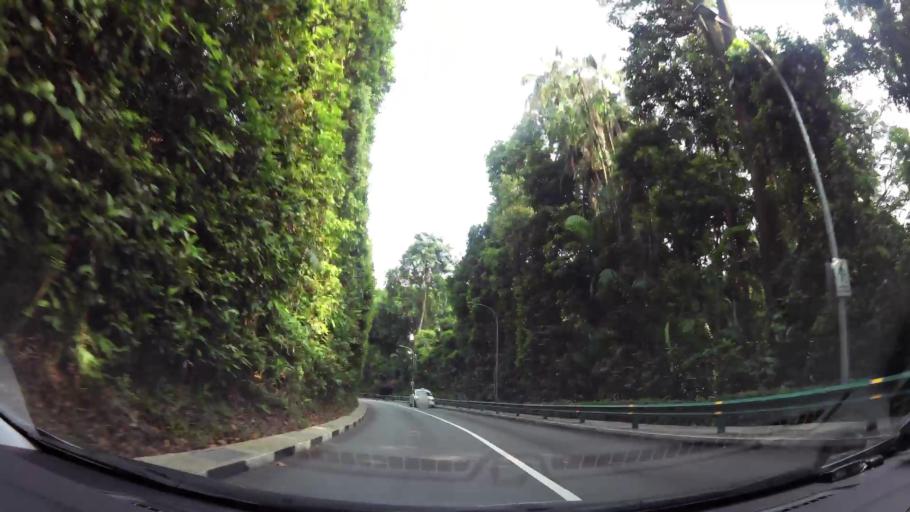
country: SG
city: Singapore
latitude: 1.2568
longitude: 103.8158
